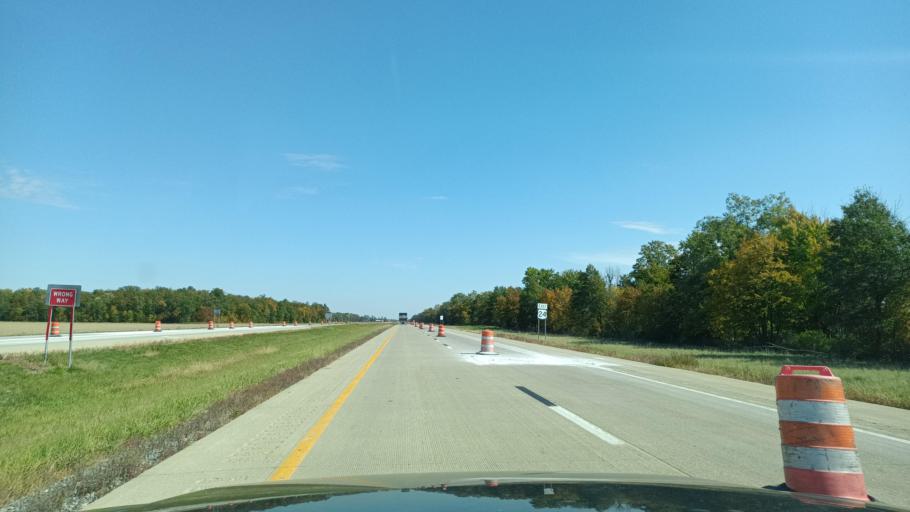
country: US
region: Ohio
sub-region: Paulding County
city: Paulding
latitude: 41.2413
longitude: -84.5145
